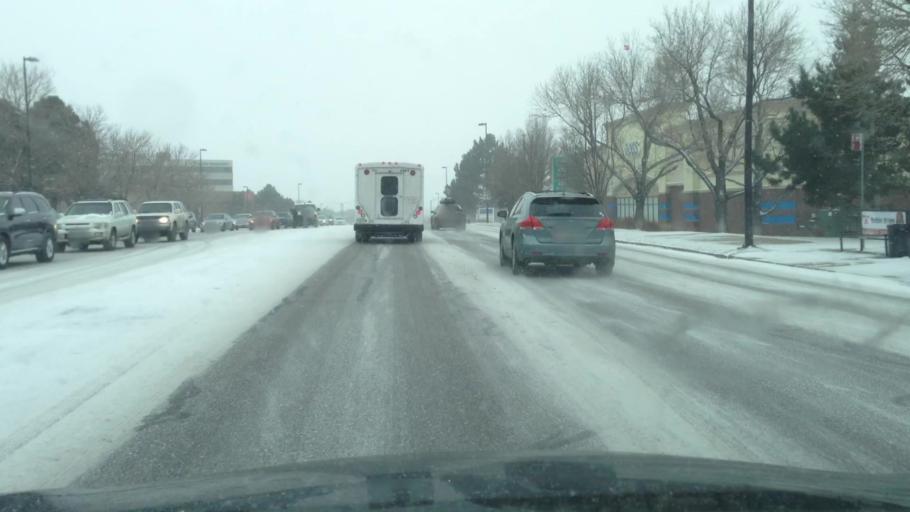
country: US
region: Colorado
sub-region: Adams County
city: Aurora
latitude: 39.6744
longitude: -104.8660
